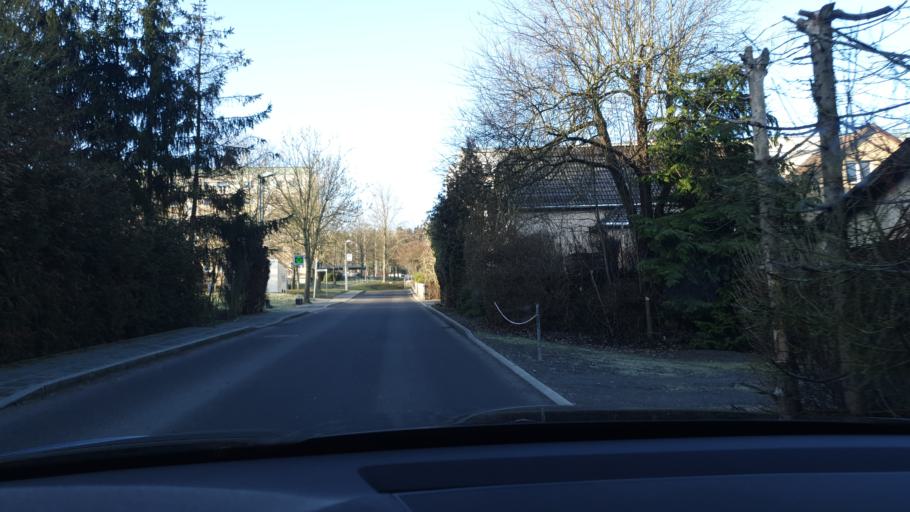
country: DE
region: Saxony
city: Floha
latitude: 50.8497
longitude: 13.0713
